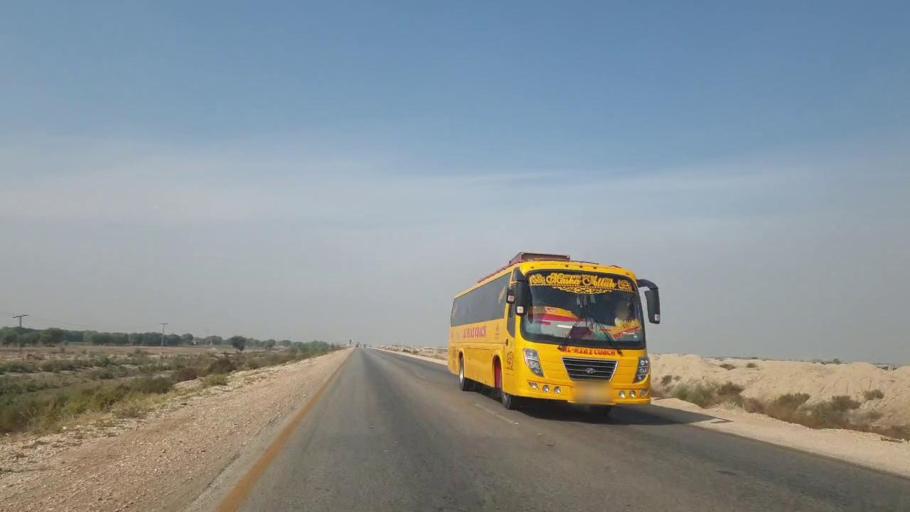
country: PK
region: Sindh
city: Sann
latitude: 25.9372
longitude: 68.2058
